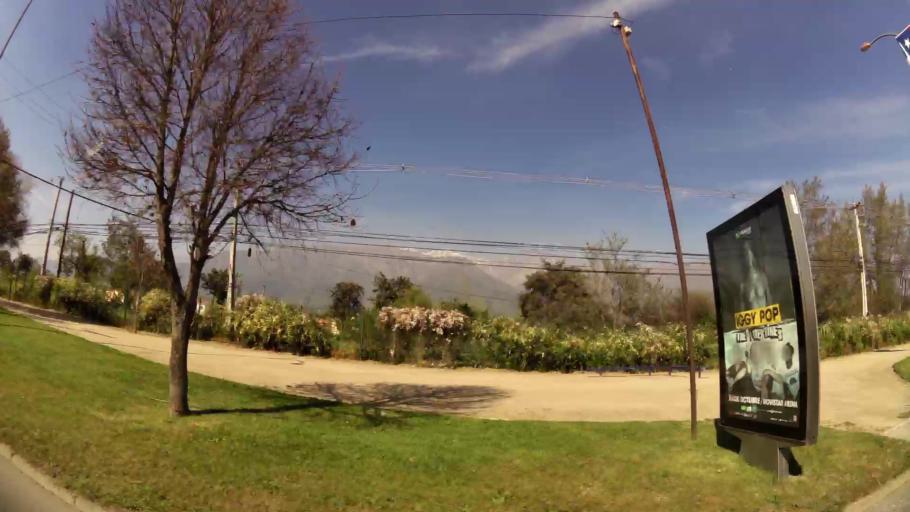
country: CL
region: Santiago Metropolitan
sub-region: Provincia de Santiago
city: Villa Presidente Frei, Nunoa, Santiago, Chile
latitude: -33.4843
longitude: -70.5584
